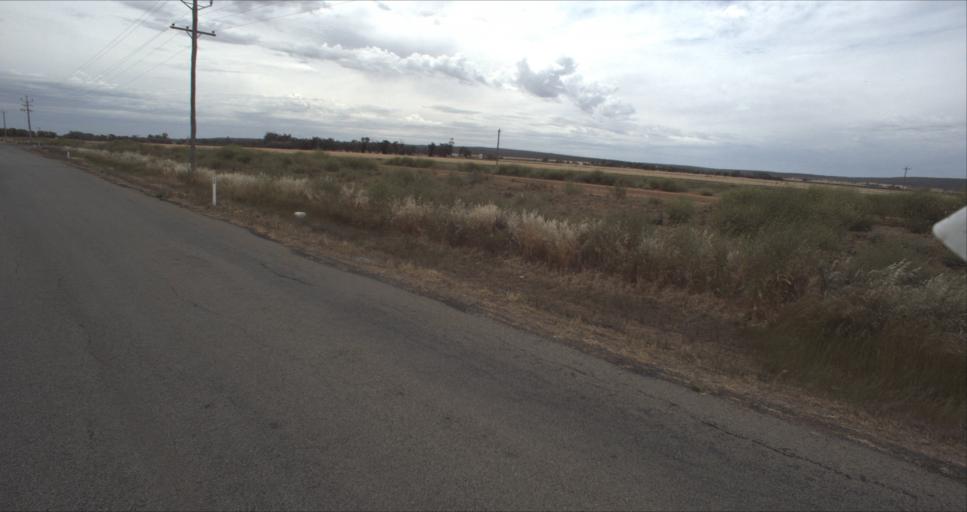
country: AU
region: New South Wales
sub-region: Leeton
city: Leeton
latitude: -34.4800
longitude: 146.3993
